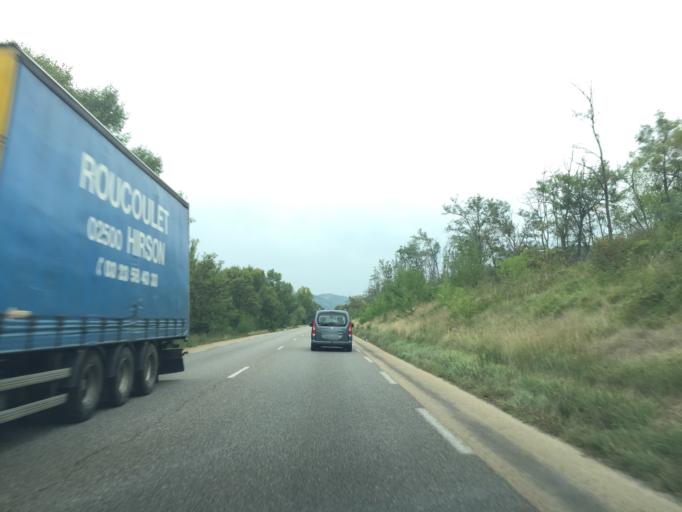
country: FR
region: Provence-Alpes-Cote d'Azur
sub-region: Departement des Alpes-de-Haute-Provence
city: Mallemoisson
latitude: 44.0594
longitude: 6.1645
